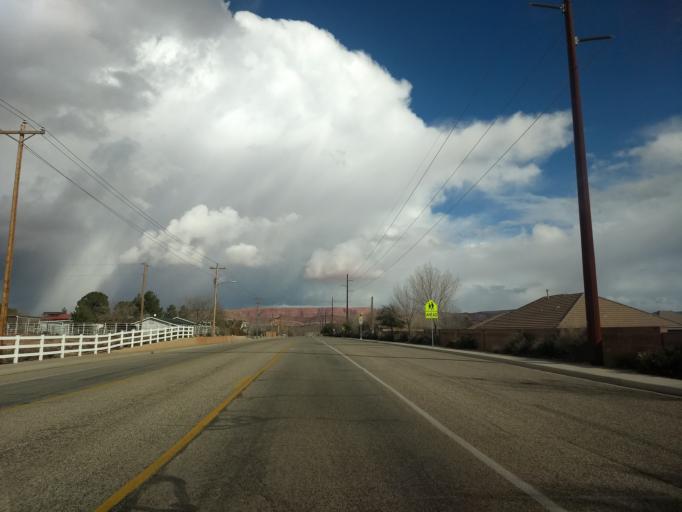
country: US
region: Utah
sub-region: Washington County
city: Saint George
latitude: 37.0668
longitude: -113.5375
